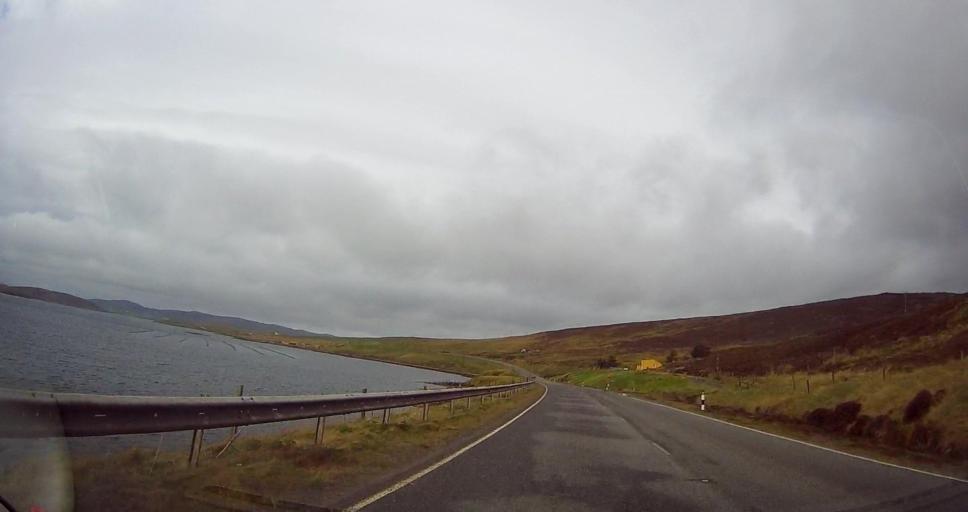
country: GB
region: Scotland
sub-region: Shetland Islands
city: Lerwick
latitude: 60.3680
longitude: -1.2945
